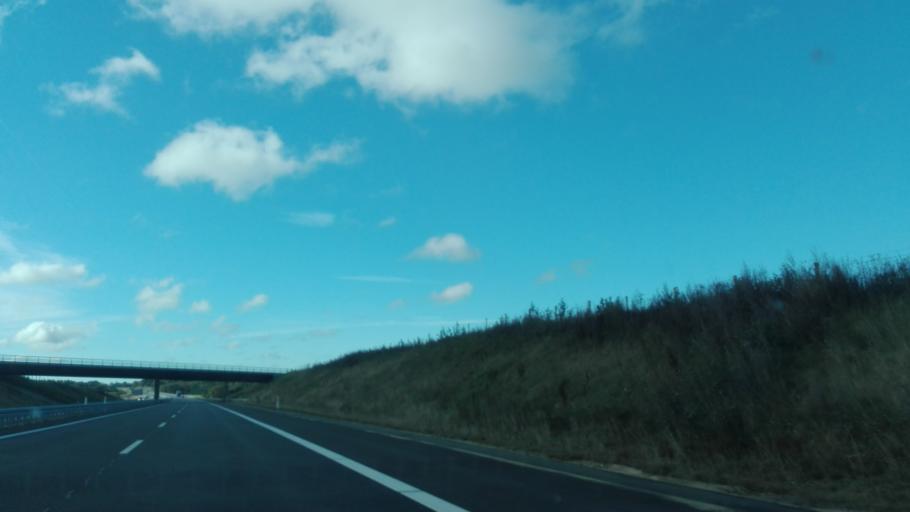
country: DK
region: Central Jutland
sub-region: Silkeborg Kommune
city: Silkeborg
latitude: 56.1912
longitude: 9.4963
